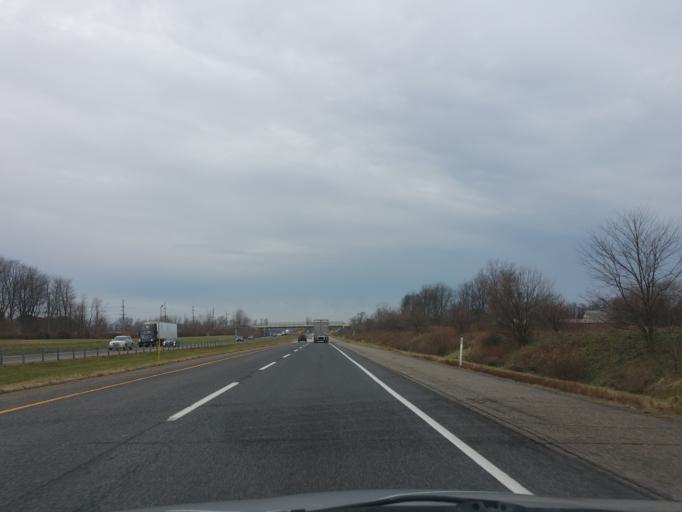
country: US
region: Indiana
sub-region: Porter County
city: South Haven
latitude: 41.5721
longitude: -87.1377
